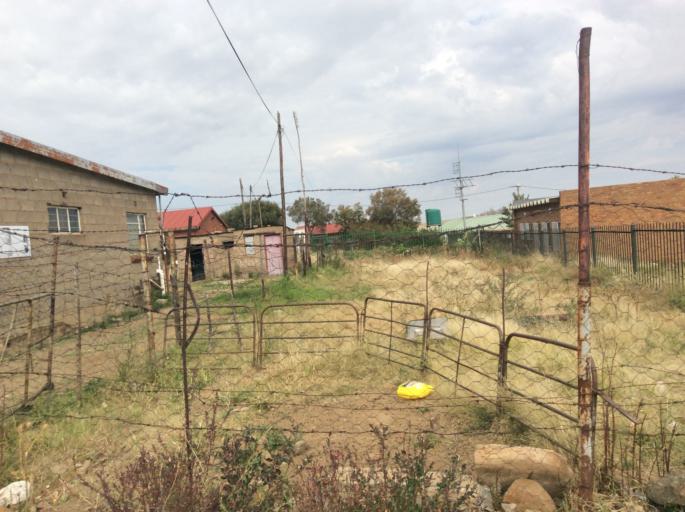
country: LS
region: Mafeteng
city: Mafeteng
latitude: -29.7197
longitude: 27.0276
